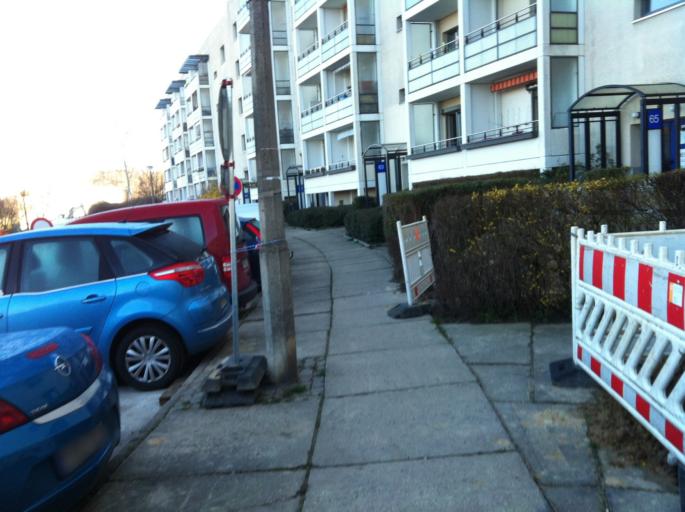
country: DE
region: Berlin
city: Kaulsdorf
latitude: 52.5260
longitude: 13.5831
